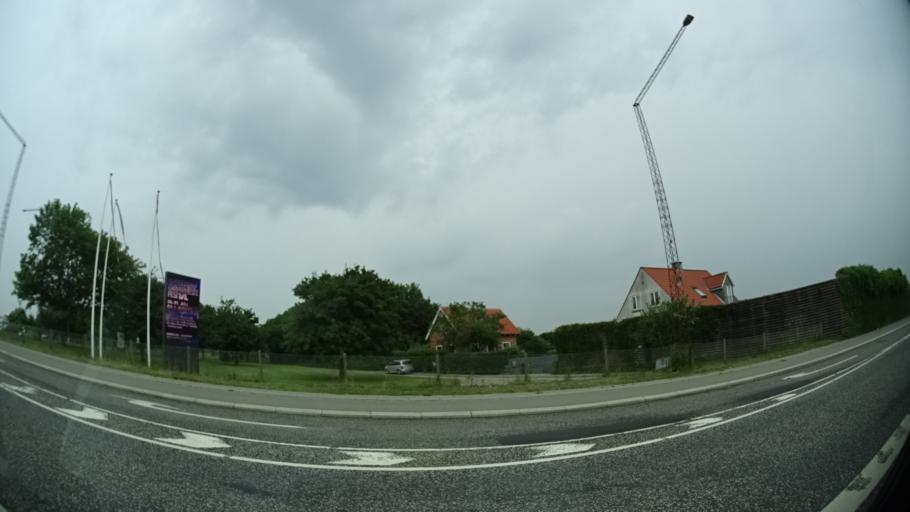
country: DK
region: Central Jutland
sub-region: Arhus Kommune
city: Arhus
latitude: 56.1960
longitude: 10.2207
